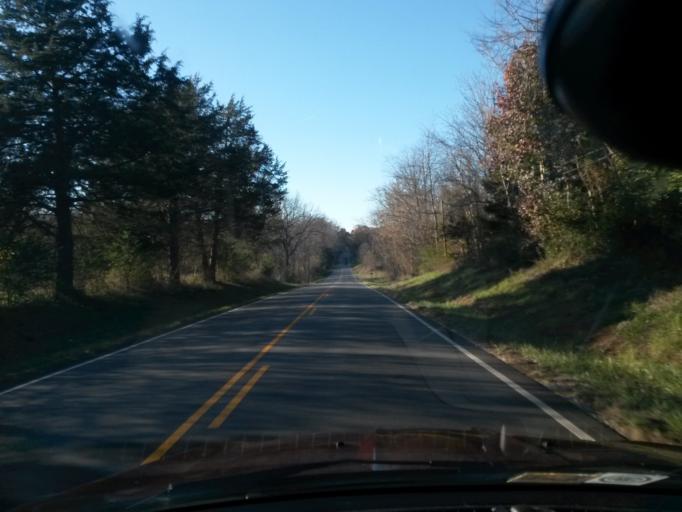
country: US
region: Virginia
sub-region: Amherst County
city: Amherst
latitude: 37.5986
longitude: -79.0595
